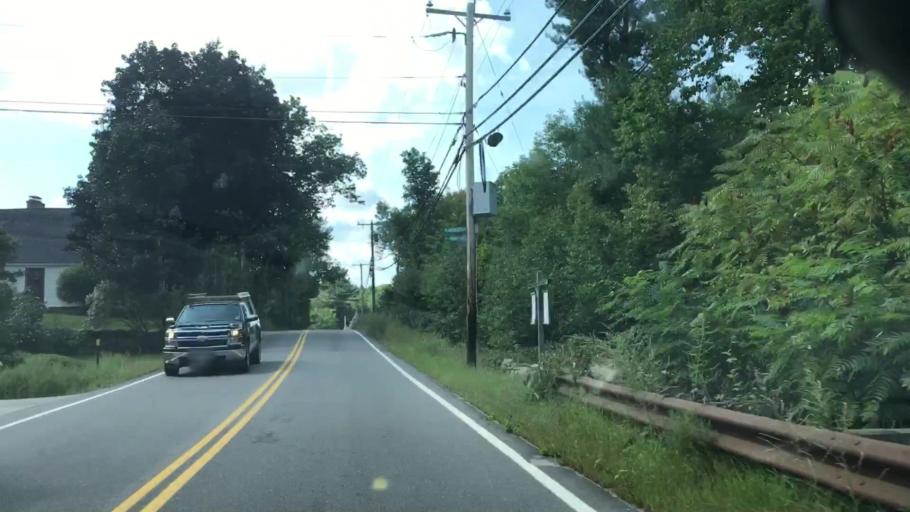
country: US
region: New Hampshire
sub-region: Hillsborough County
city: Bedford
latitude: 42.9431
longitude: -71.5284
